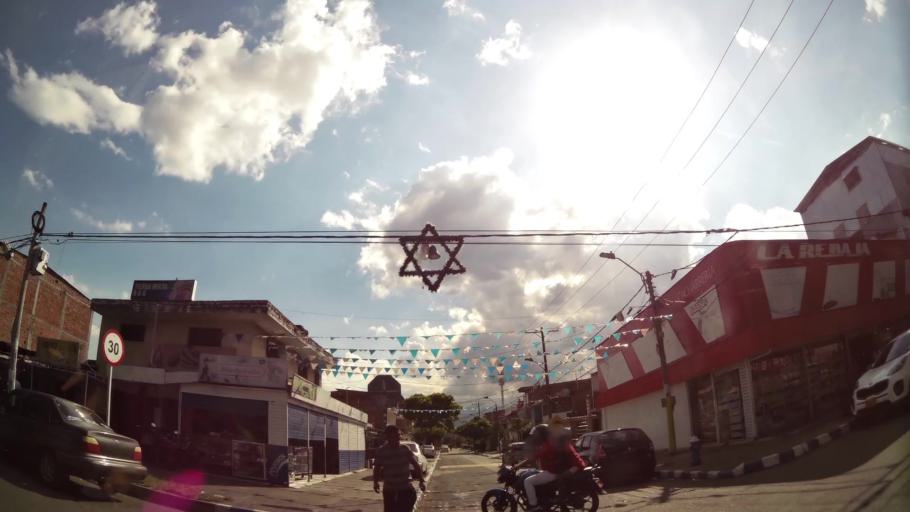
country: CO
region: Valle del Cauca
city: Cali
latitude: 3.4188
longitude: -76.5075
